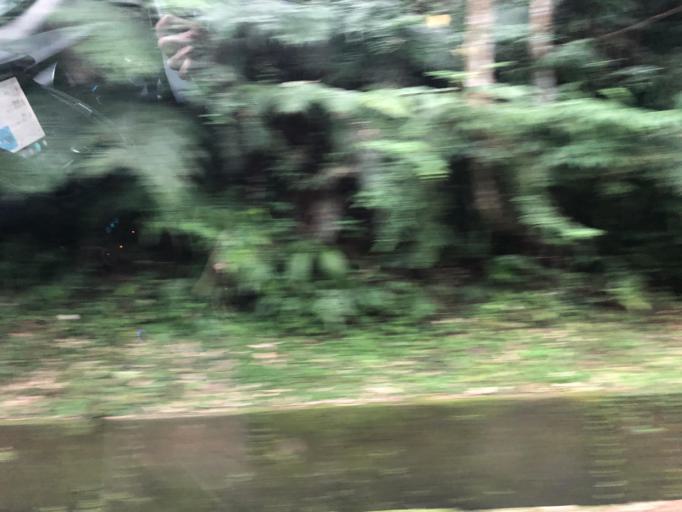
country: TW
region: Taipei
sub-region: Taipei
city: Banqiao
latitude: 24.8899
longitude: 121.4307
